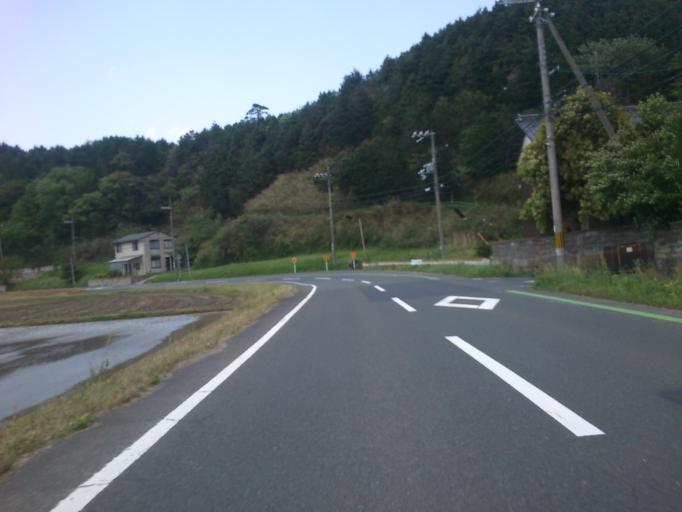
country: JP
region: Kyoto
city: Miyazu
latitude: 35.7252
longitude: 135.1067
